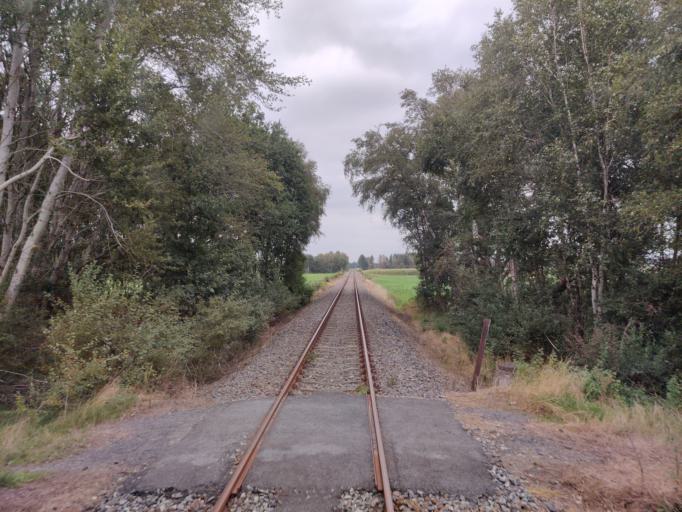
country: DE
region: Lower Saxony
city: Worpswede
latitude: 53.2799
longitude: 8.9655
